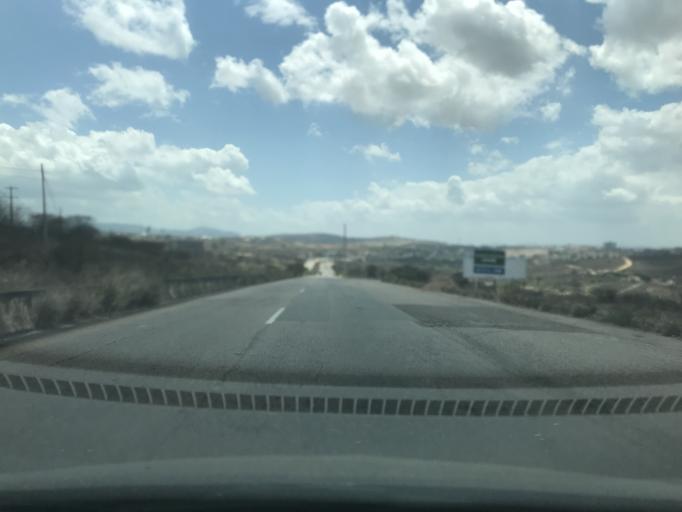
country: BR
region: Pernambuco
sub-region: Caruaru
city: Caruaru
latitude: -8.3068
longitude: -35.9402
